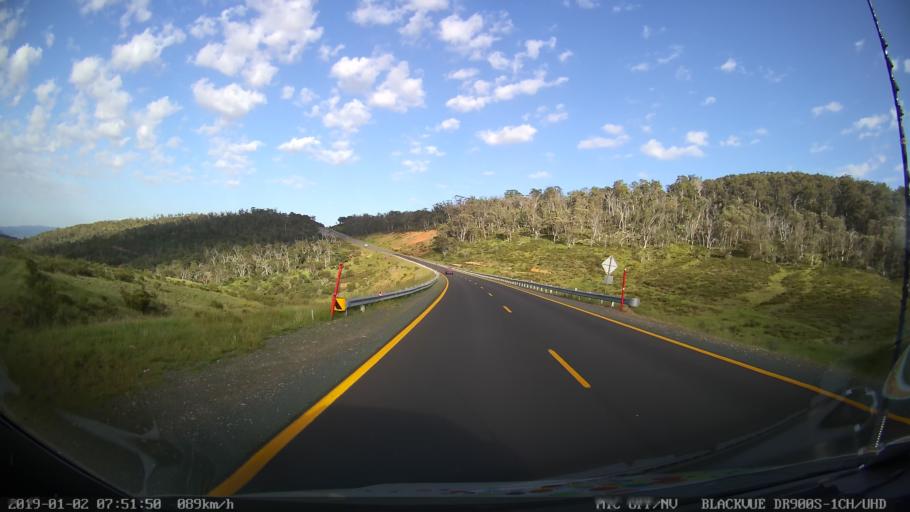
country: AU
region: New South Wales
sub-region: Tumut Shire
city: Tumut
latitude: -35.7147
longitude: 148.5274
